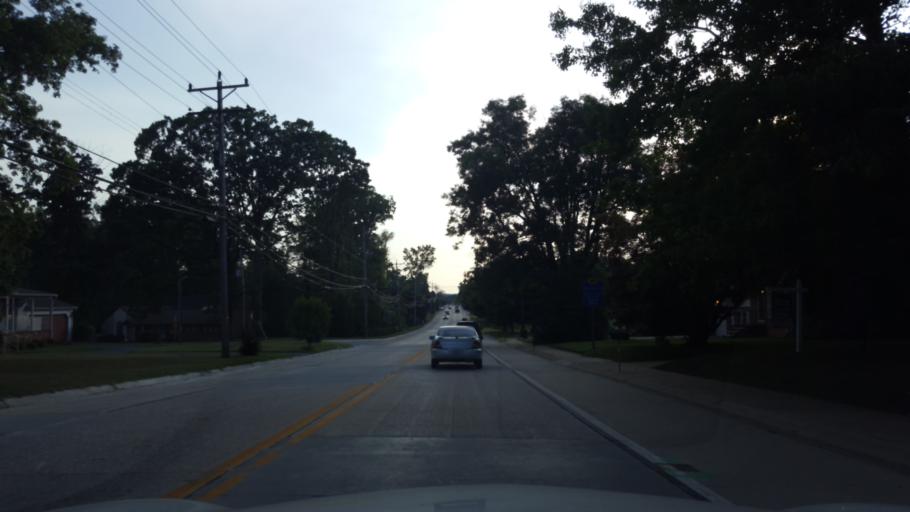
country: US
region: Delaware
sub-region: New Castle County
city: Pike Creek Valley
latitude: 39.7370
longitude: -75.6518
